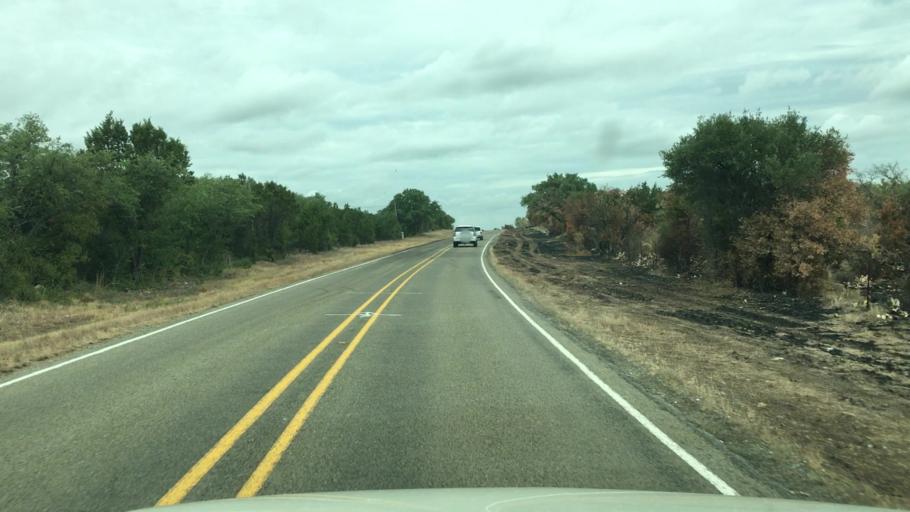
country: US
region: Texas
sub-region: Llano County
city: Horseshoe Bay
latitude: 30.4847
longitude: -98.4296
